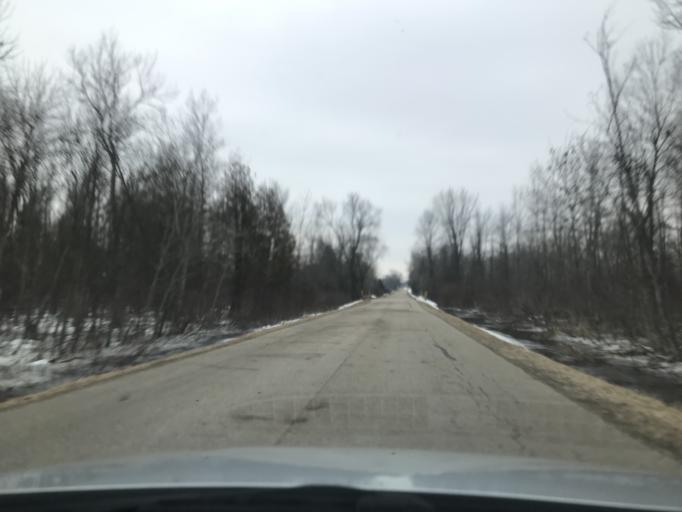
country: US
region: Wisconsin
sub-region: Marinette County
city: Peshtigo
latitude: 45.1300
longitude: -88.0076
